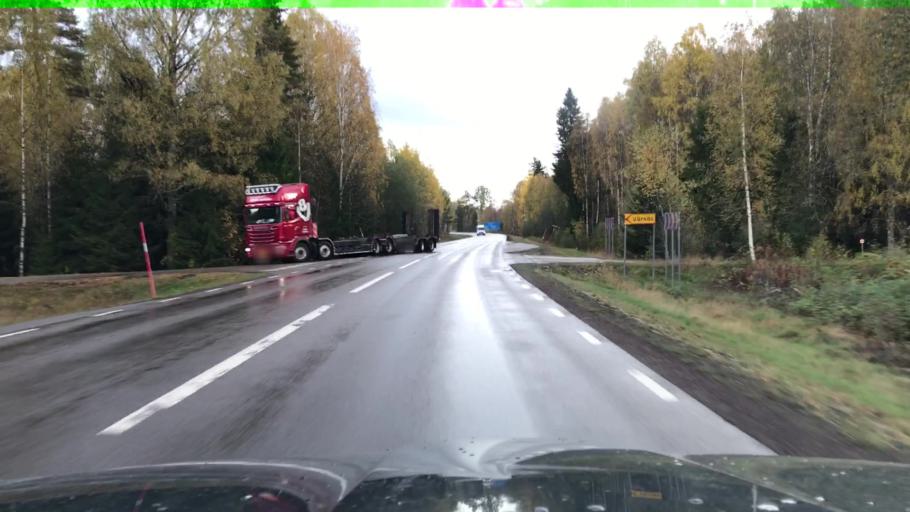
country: SE
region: Vaermland
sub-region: Hagfors Kommun
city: Ekshaerad
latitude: 60.4277
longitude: 13.2491
